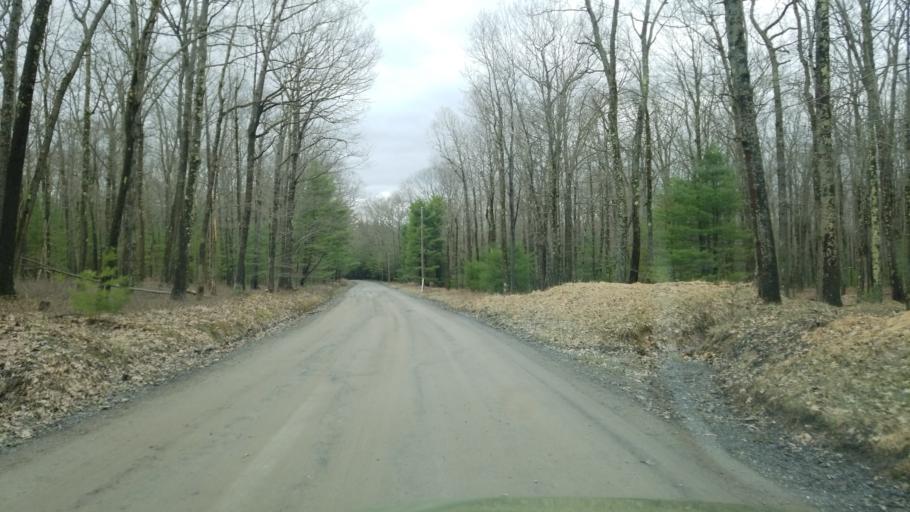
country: US
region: Pennsylvania
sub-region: Clearfield County
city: Shiloh
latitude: 41.1636
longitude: -78.3352
